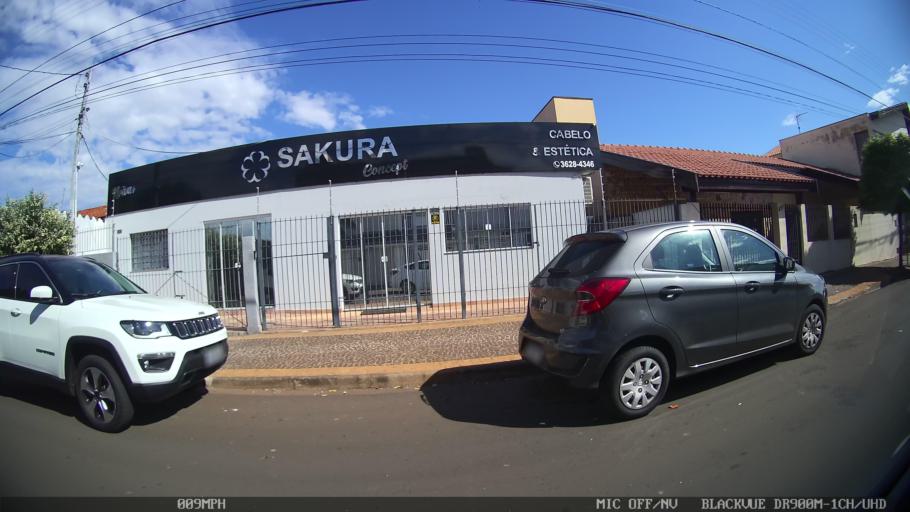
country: BR
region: Sao Paulo
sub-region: Americana
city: Americana
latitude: -22.7420
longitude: -47.3726
